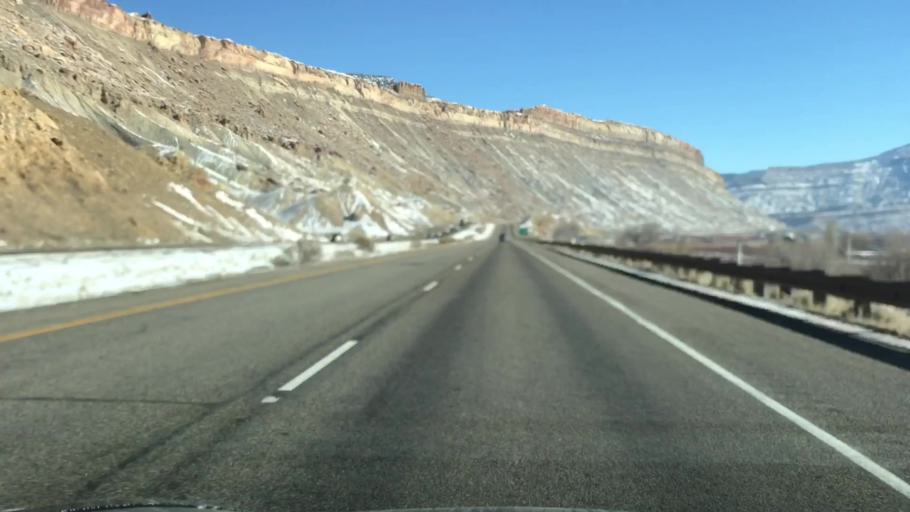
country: US
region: Colorado
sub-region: Mesa County
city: Palisade
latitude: 39.1181
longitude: -108.3864
